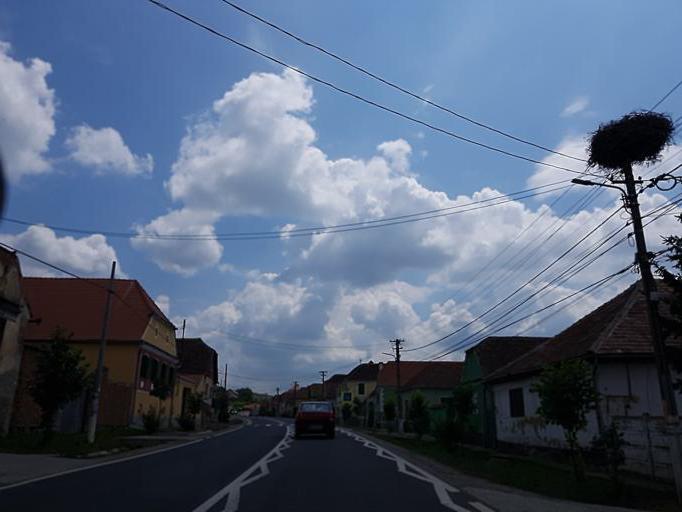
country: RO
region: Sibiu
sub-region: Comuna Slimnic
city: Slimnic
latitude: 45.9573
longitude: 24.1678
